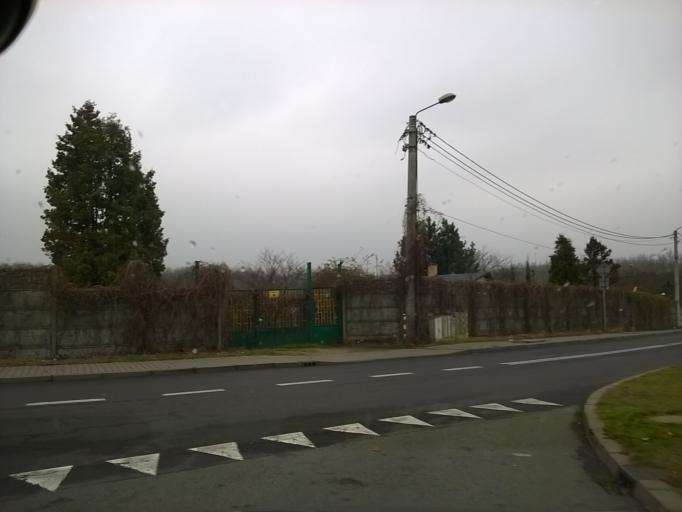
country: PL
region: Silesian Voivodeship
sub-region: Swietochlowice
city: Swietochlowice
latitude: 50.2600
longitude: 18.9395
